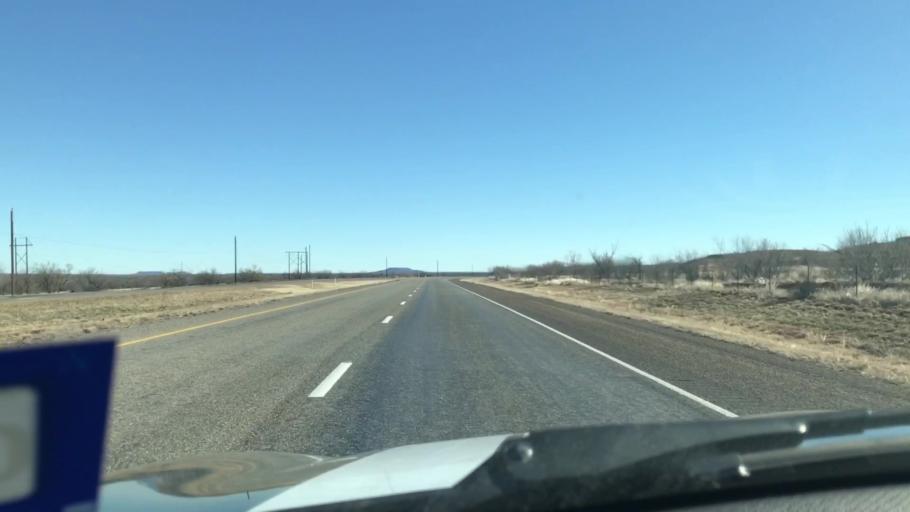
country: US
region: Texas
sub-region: Garza County
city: Post
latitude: 33.0626
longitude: -101.2204
